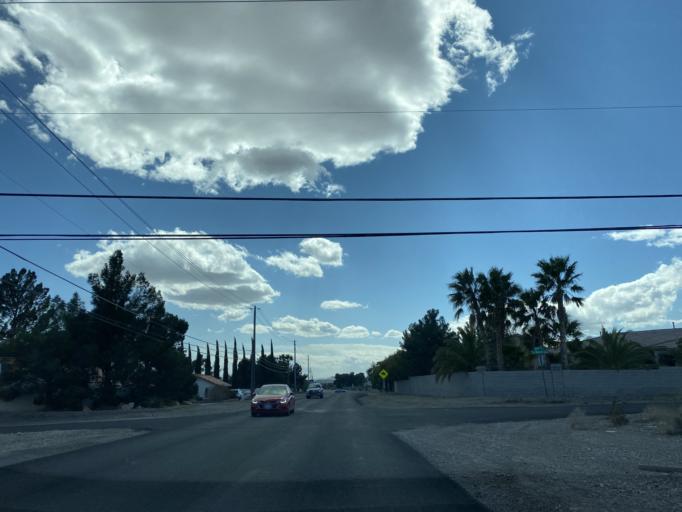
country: US
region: Nevada
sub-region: Clark County
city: Summerlin South
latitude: 36.2649
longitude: -115.2884
